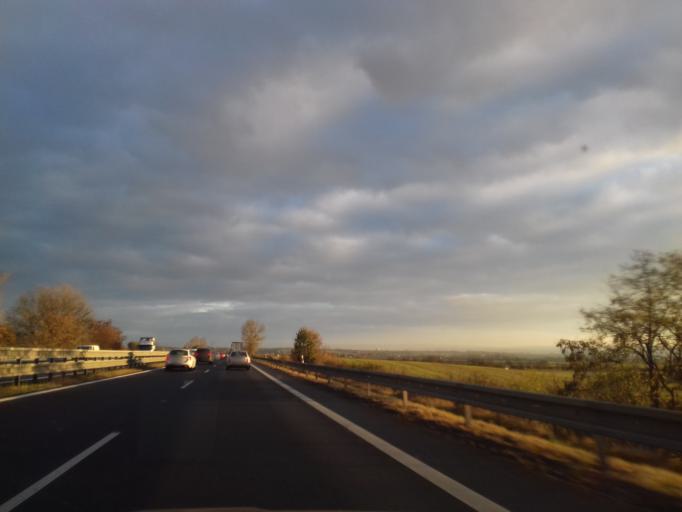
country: CZ
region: Olomoucky
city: Smrzice
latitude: 49.5049
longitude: 17.1432
